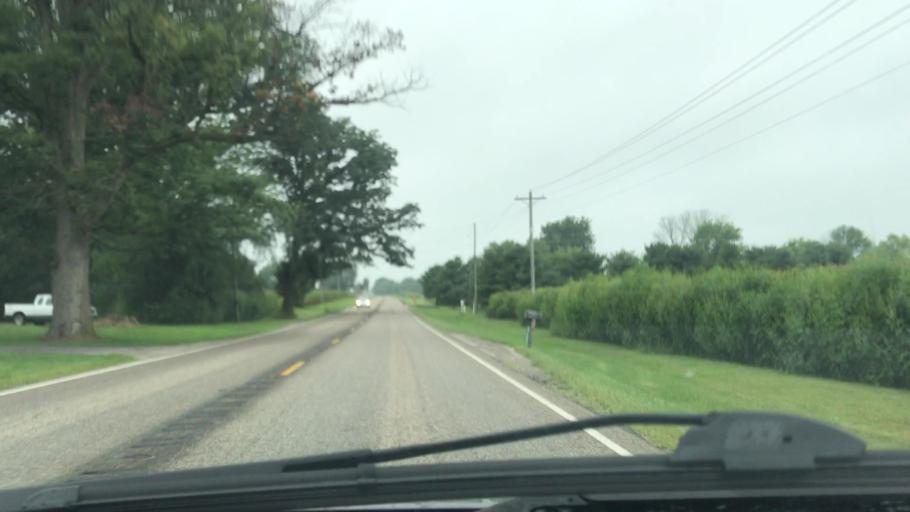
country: US
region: Indiana
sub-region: Hamilton County
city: Sheridan
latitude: 40.1278
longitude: -86.3419
